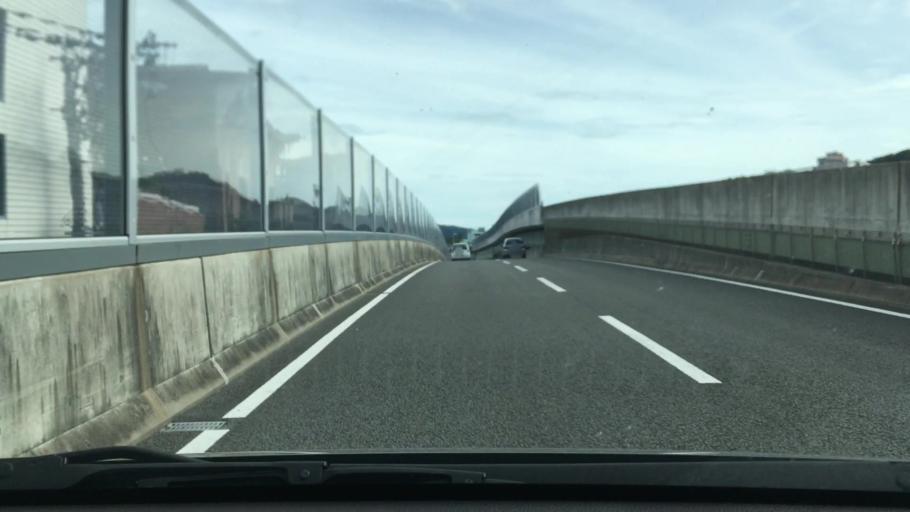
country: JP
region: Nagasaki
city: Nagasaki-shi
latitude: 32.7643
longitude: 129.8621
